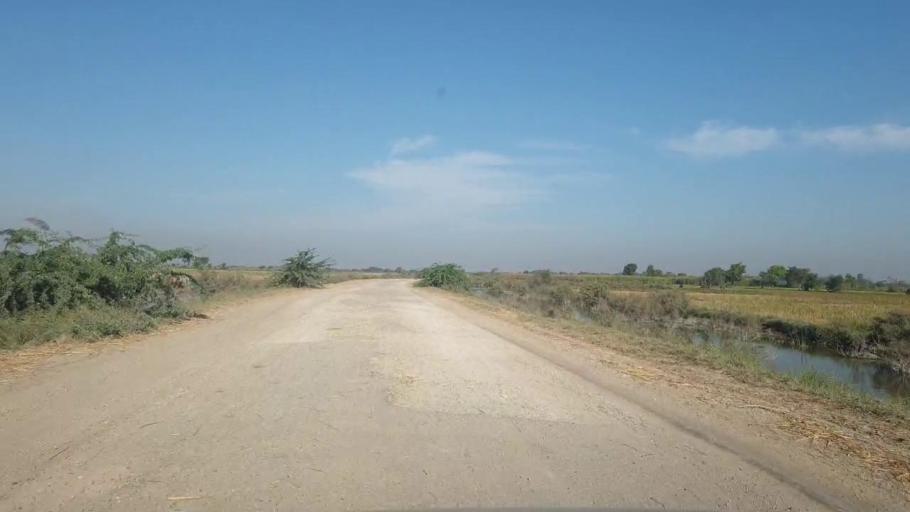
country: PK
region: Sindh
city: Talhar
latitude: 24.9158
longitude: 68.8038
